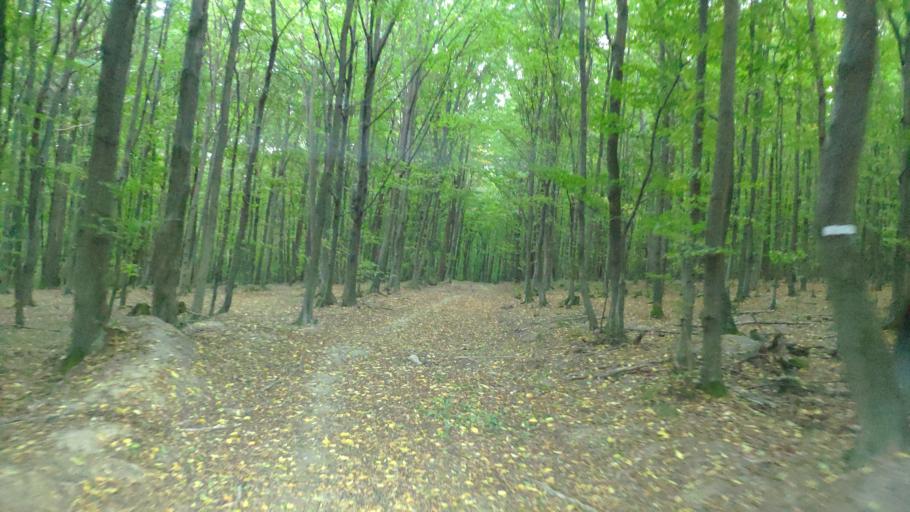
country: SK
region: Kosicky
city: Kosice
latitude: 48.6994
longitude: 21.1949
